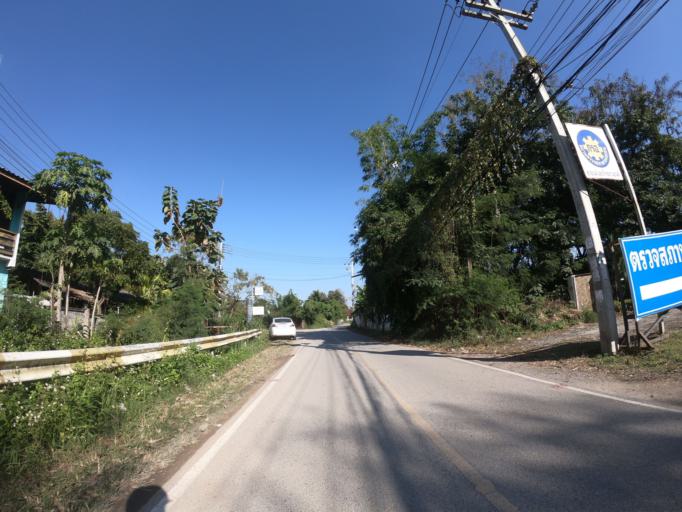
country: TH
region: Chiang Mai
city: Chiang Mai
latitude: 18.7493
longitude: 98.9646
